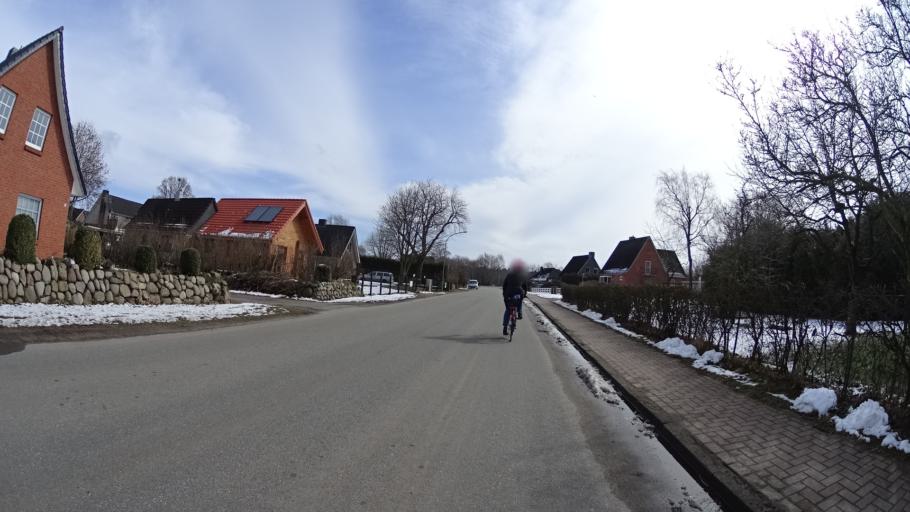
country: DE
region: Schleswig-Holstein
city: Gross Kummerfeld
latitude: 54.0284
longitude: 10.1180
